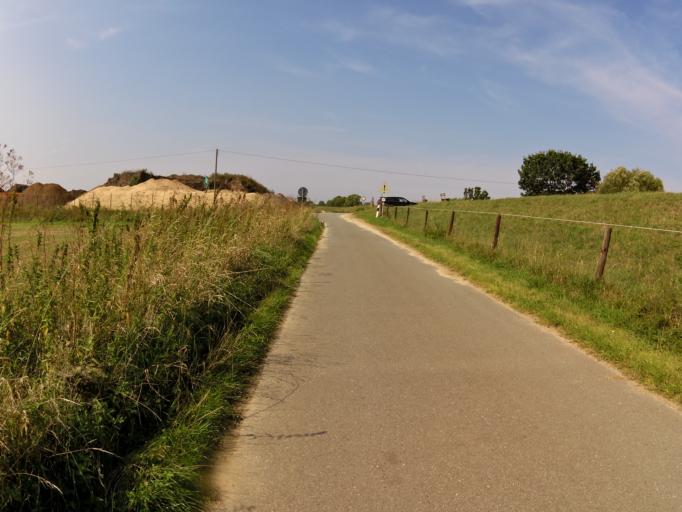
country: DE
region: Lower Saxony
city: Riede
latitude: 53.0040
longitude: 8.9047
